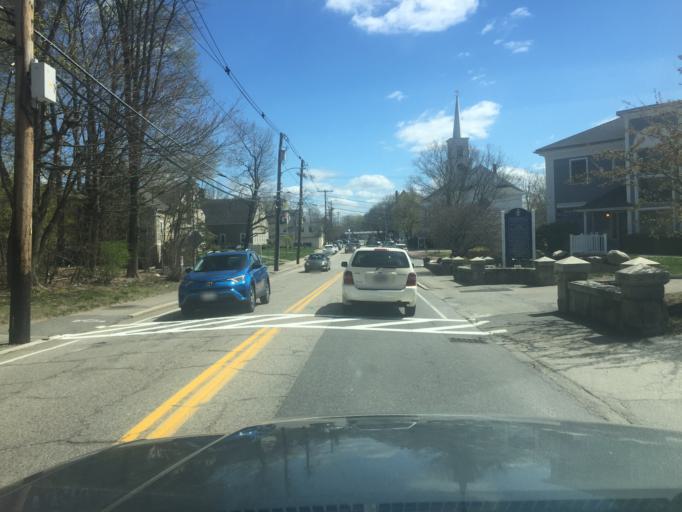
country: US
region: Massachusetts
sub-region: Norfolk County
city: Medfield
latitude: 42.1884
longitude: -71.3072
